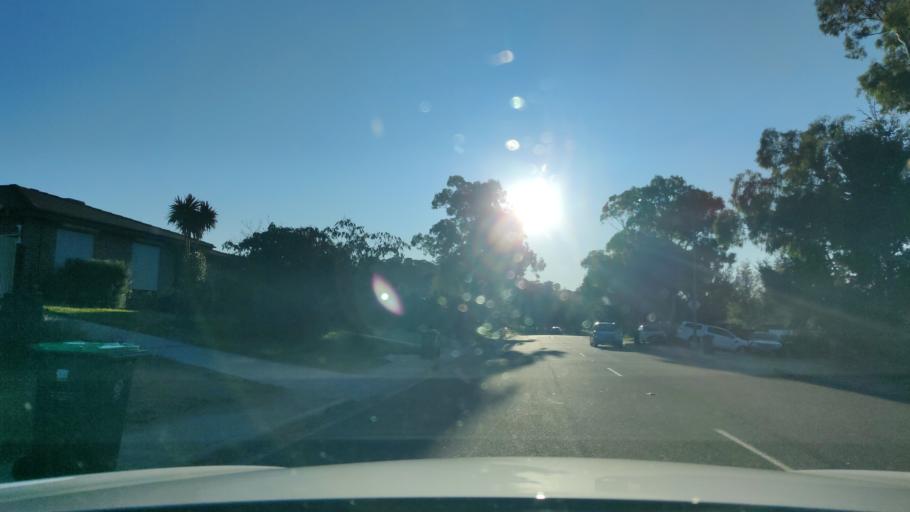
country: AU
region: Australian Capital Territory
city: Macarthur
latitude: -35.4459
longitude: 149.1187
